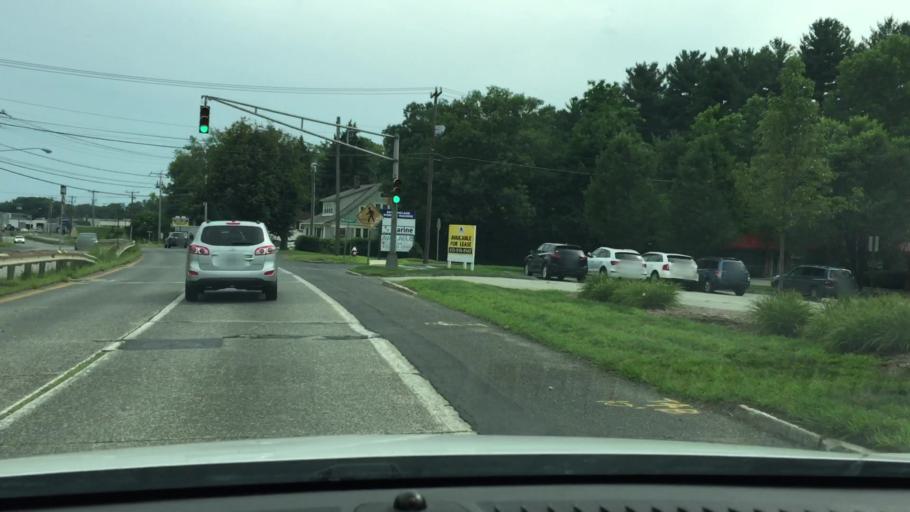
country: US
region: Massachusetts
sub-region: Hampden County
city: Chicopee
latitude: 42.1491
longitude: -72.6307
